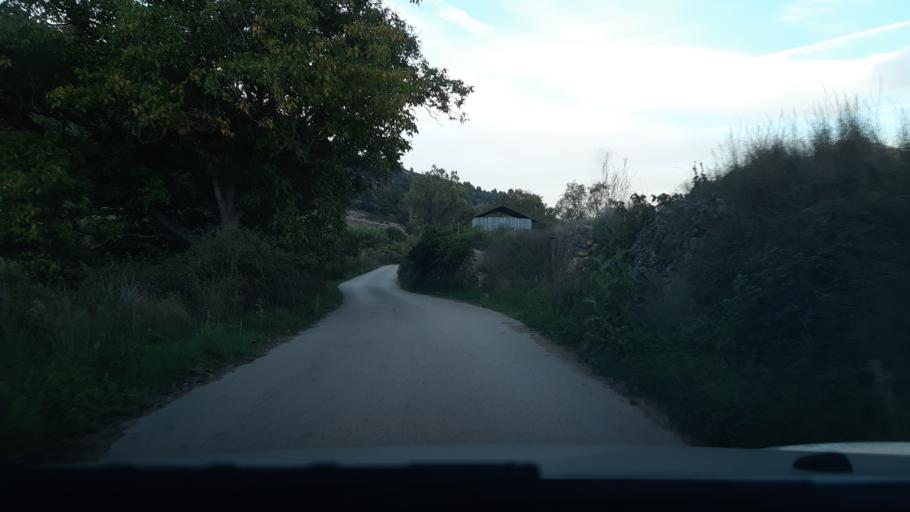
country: ES
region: Aragon
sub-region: Provincia de Teruel
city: Valderrobres
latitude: 40.8393
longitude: 0.1928
